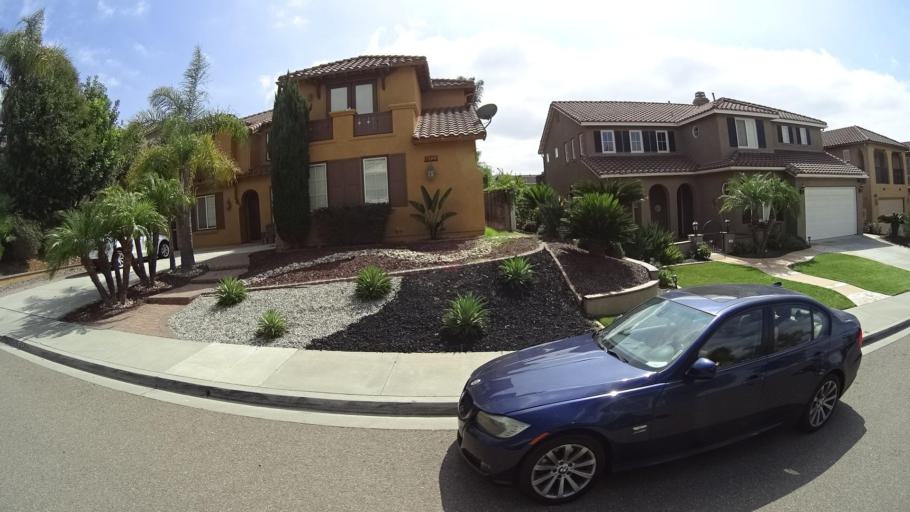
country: US
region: California
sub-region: San Diego County
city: Fairbanks Ranch
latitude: 33.0112
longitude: -117.1082
